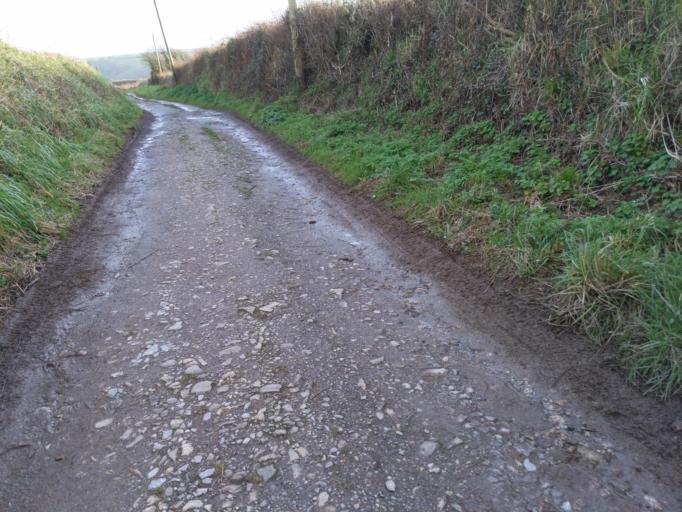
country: GB
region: England
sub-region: Devon
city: Wembury
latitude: 50.3184
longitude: -4.0624
